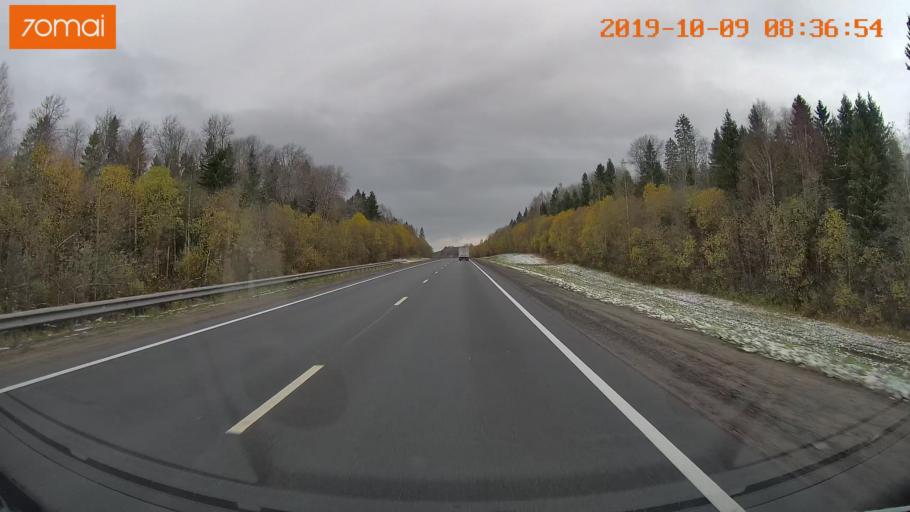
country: RU
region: Vologda
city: Gryazovets
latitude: 58.9332
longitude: 40.1758
